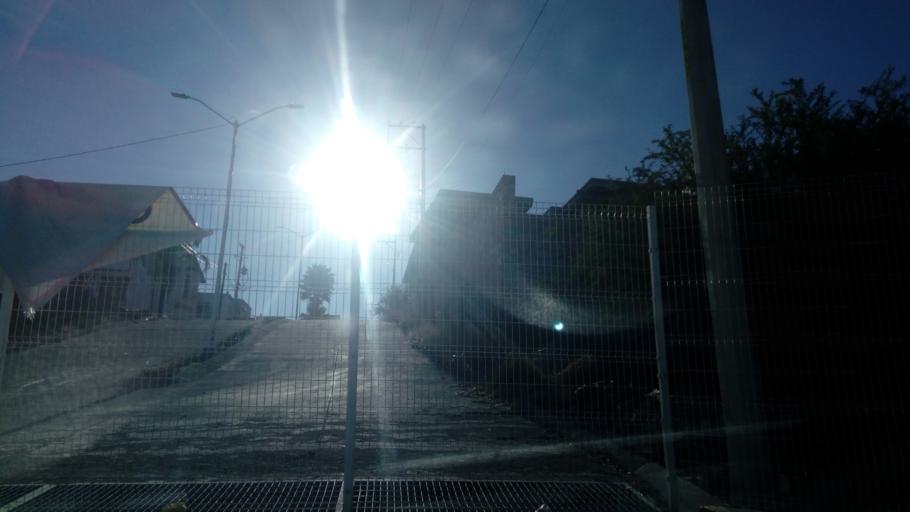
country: MX
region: Durango
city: Victoria de Durango
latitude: 24.0146
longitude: -104.6921
